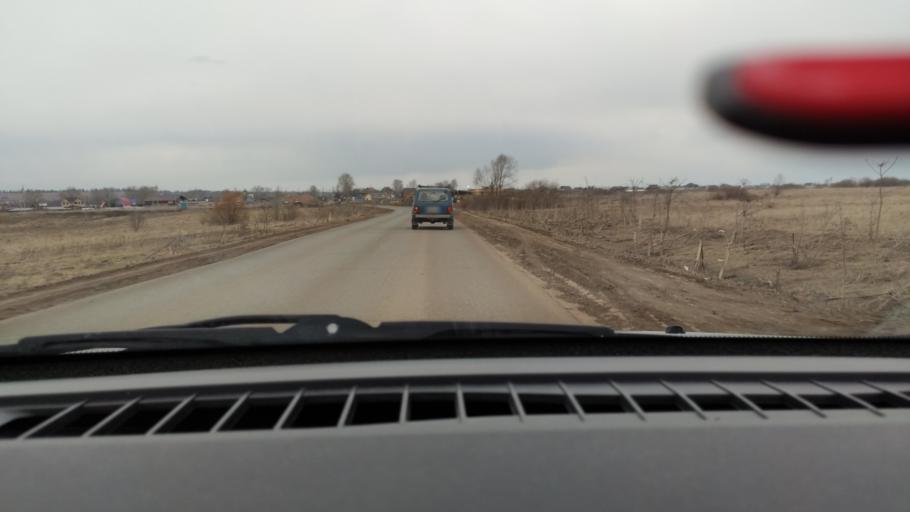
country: RU
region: Perm
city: Kultayevo
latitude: 57.9043
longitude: 55.9921
